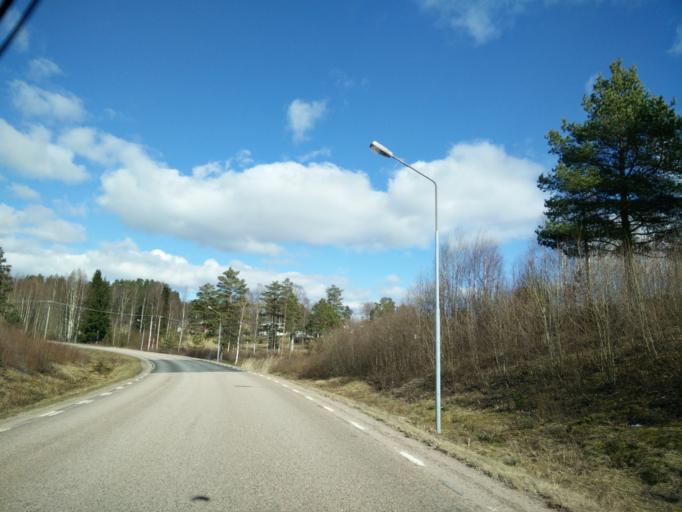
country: SE
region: Vaermland
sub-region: Hagfors Kommun
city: Hagfors
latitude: 59.8817
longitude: 13.7133
